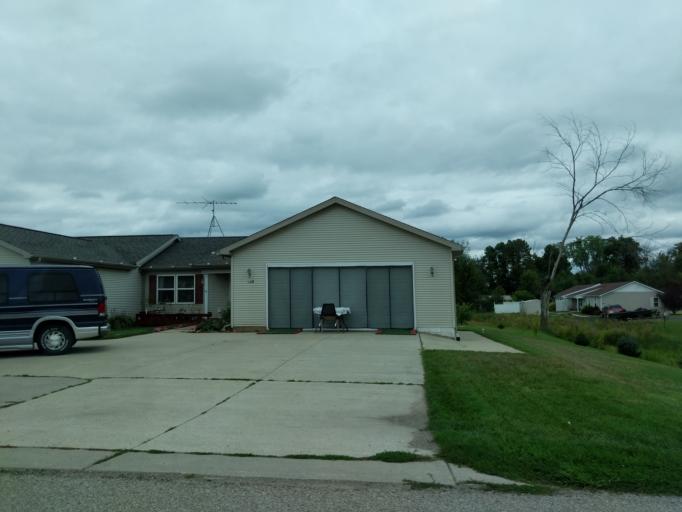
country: US
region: Michigan
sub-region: Tuscola County
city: Caro
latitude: 43.3367
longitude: -83.3604
